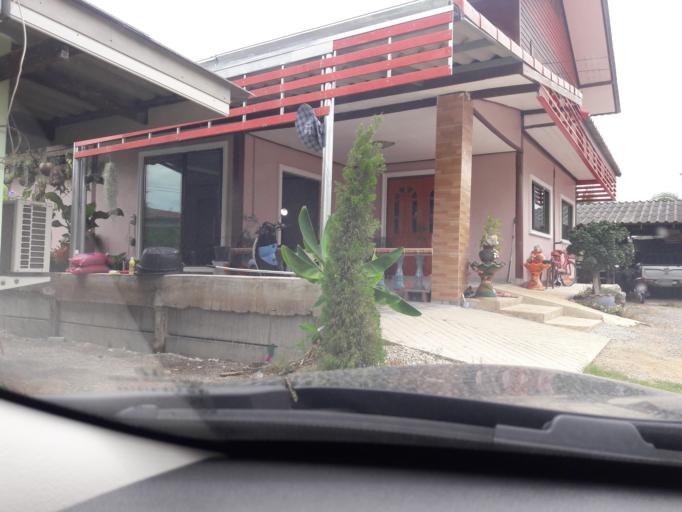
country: TH
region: Ratchaburi
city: Bang Phae
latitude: 13.6029
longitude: 99.9058
